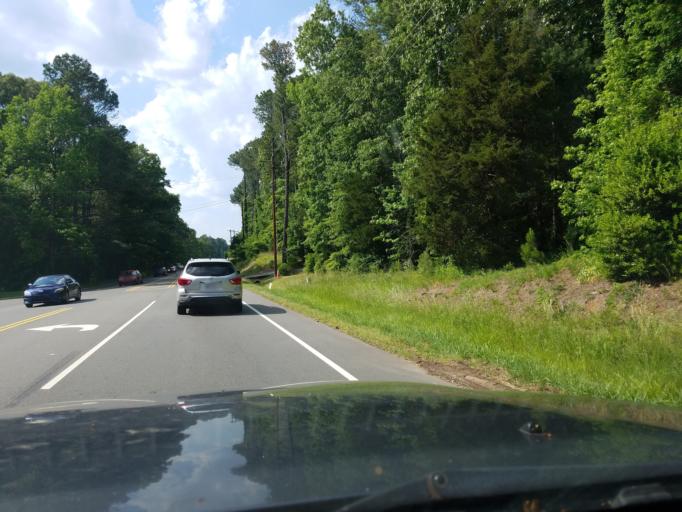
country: US
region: North Carolina
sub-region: Durham County
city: Durham
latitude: 35.9366
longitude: -78.9627
